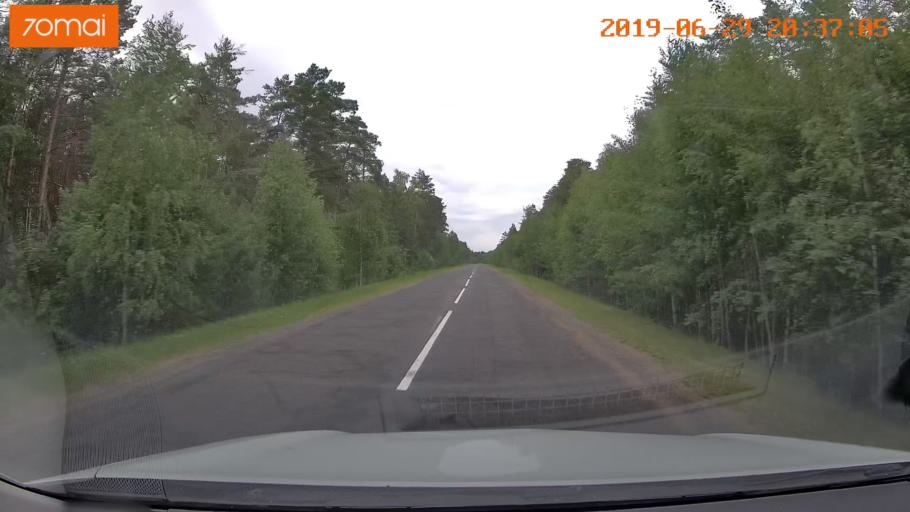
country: BY
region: Brest
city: Hantsavichy
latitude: 52.5336
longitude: 26.3631
